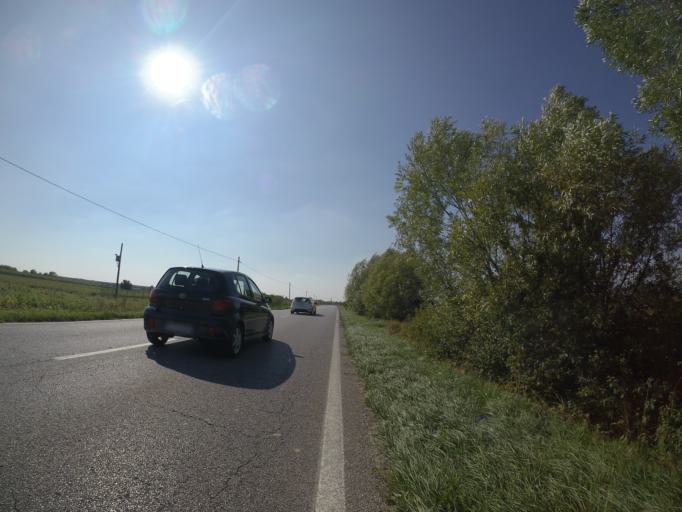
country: IT
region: Friuli Venezia Giulia
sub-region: Provincia di Udine
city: Muzzana del Turgnano
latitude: 45.8149
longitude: 13.1410
